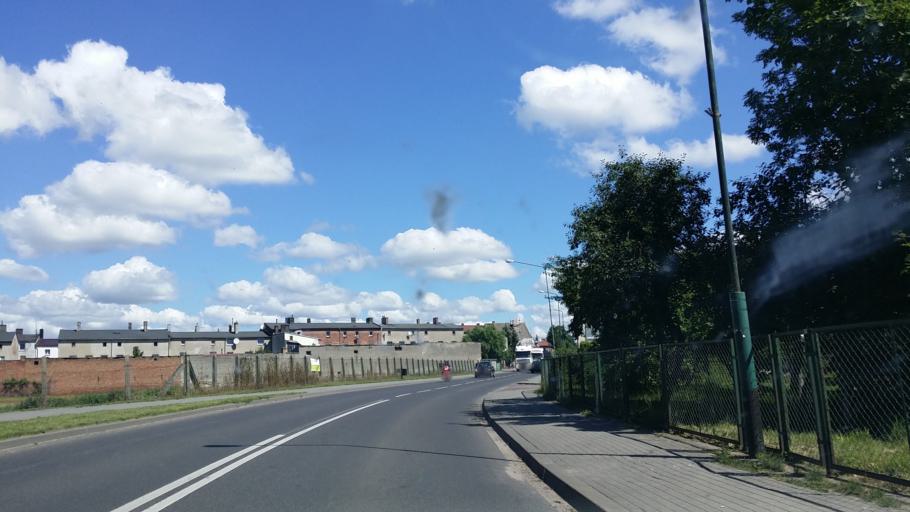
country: PL
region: West Pomeranian Voivodeship
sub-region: Powiat swidwinski
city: Swidwin
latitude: 53.7773
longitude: 15.7772
